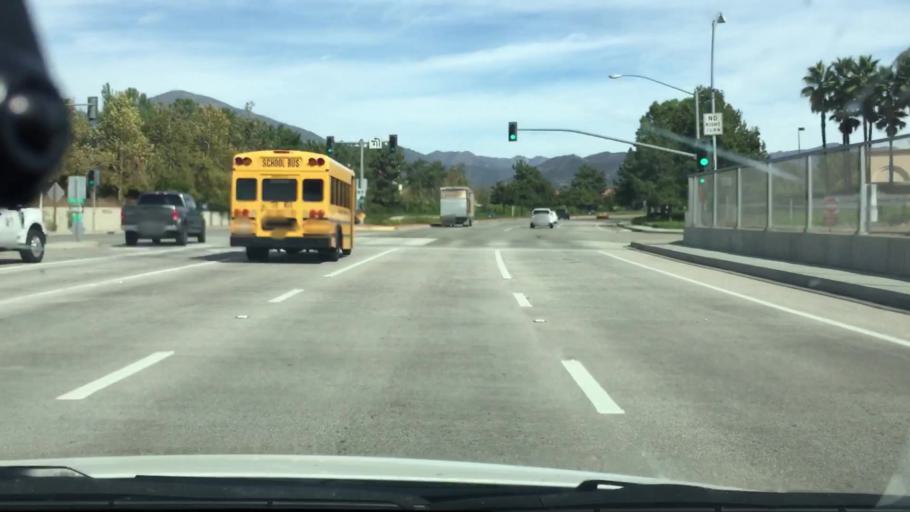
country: US
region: California
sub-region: Orange County
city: Rancho Santa Margarita
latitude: 33.6428
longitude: -117.6036
